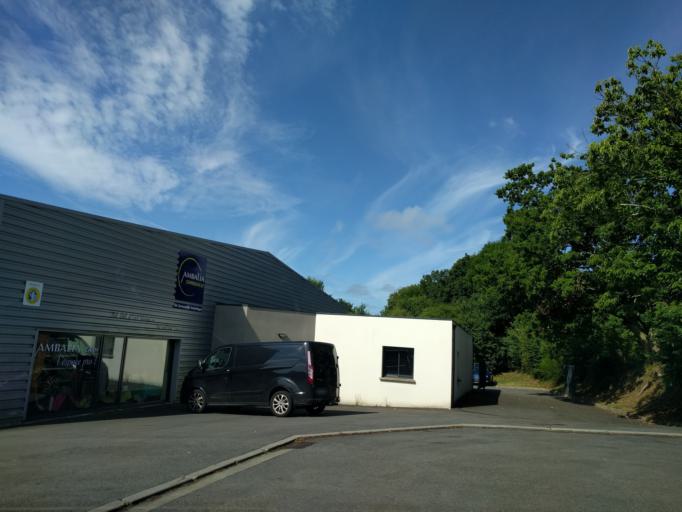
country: FR
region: Brittany
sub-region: Departement du Finistere
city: Quimper
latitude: 48.0074
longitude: -4.0684
